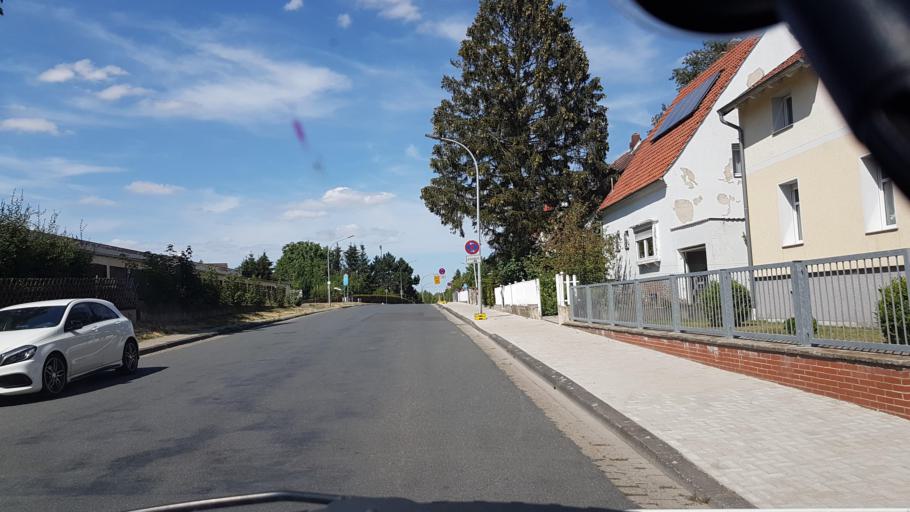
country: DE
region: Lower Saxony
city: Schoningen
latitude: 52.1423
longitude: 10.9747
